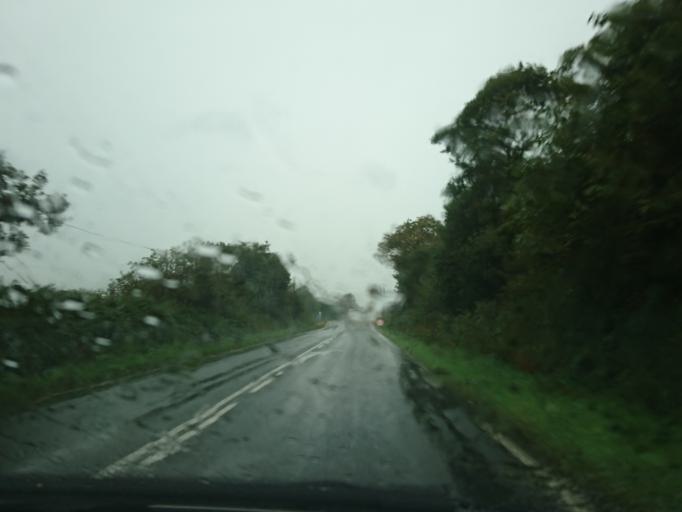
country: FR
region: Brittany
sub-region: Departement du Finistere
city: Plabennec
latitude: 48.4771
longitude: -4.4385
